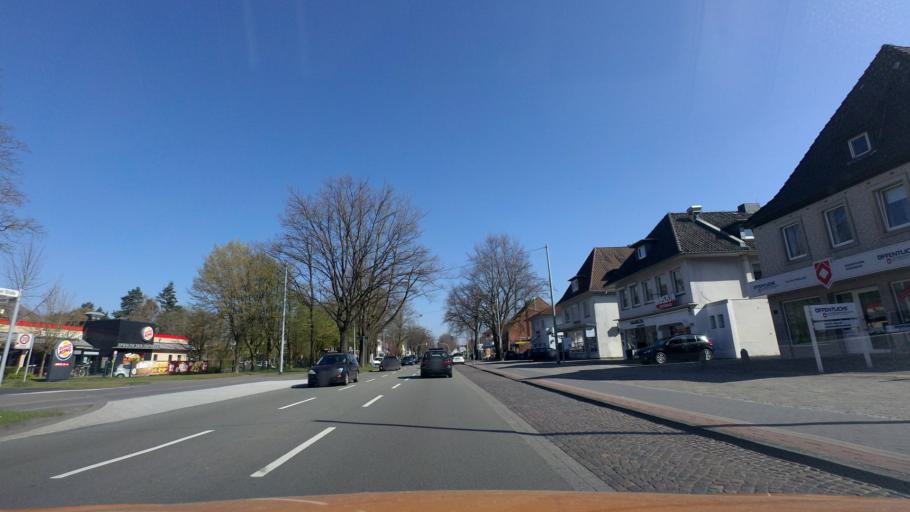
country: DE
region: Lower Saxony
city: Oldenburg
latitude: 53.1118
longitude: 8.2107
